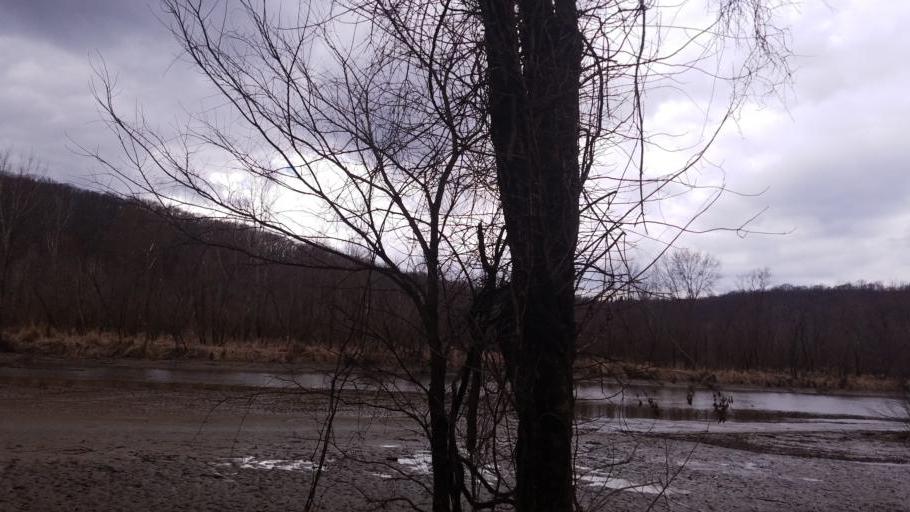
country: US
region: Ohio
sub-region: Muskingum County
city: Frazeysburg
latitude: 40.0405
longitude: -82.1327
